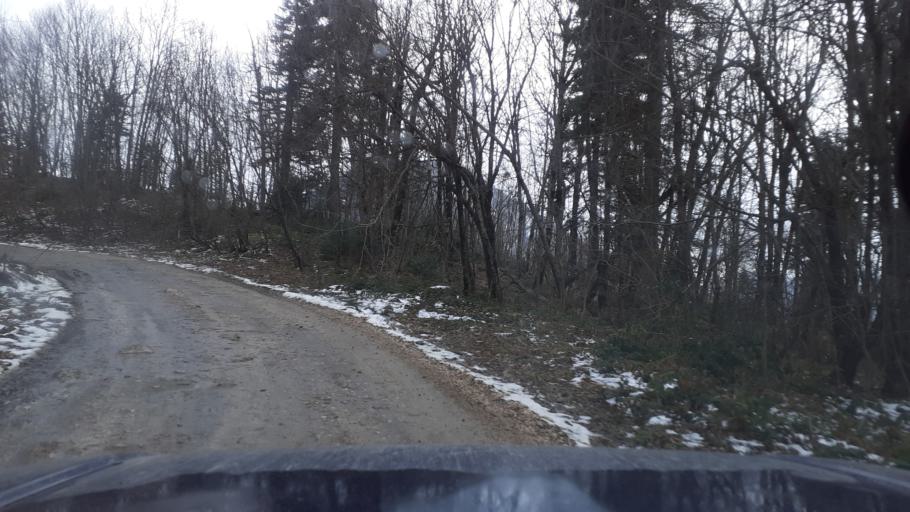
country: RU
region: Krasnodarskiy
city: Neftegorsk
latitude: 44.0788
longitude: 39.7425
